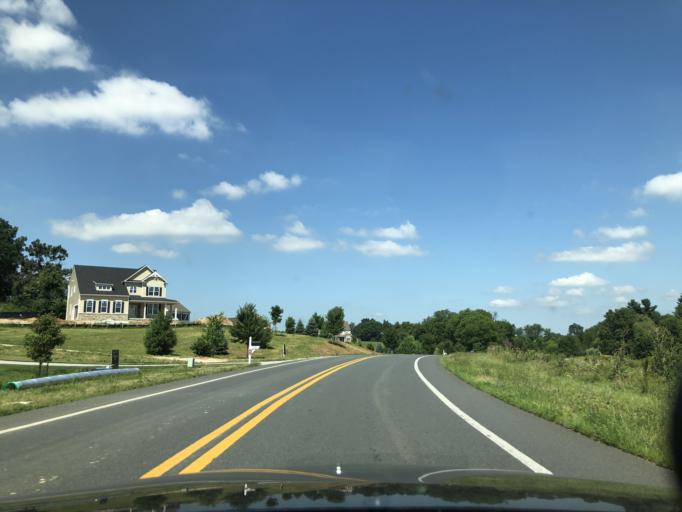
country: US
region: Maryland
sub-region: Carroll County
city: Westminster
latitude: 39.6052
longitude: -76.9745
